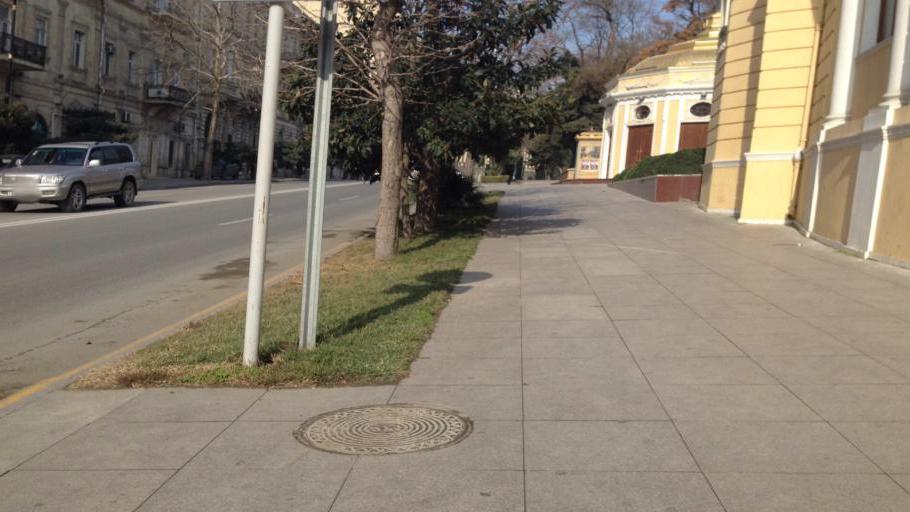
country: AZ
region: Baki
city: Badamdar
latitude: 40.3641
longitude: 49.8312
